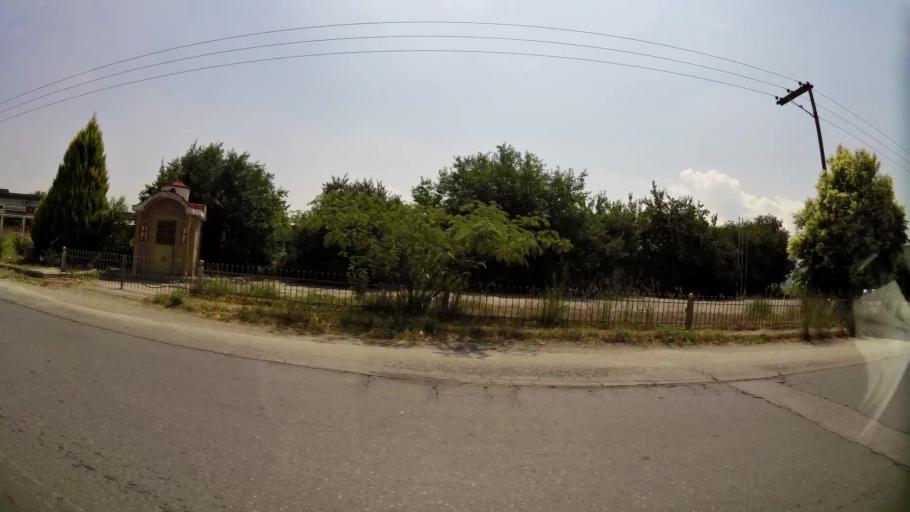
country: GR
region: Central Macedonia
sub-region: Nomos Imathias
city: Veroia
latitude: 40.5255
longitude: 22.2156
